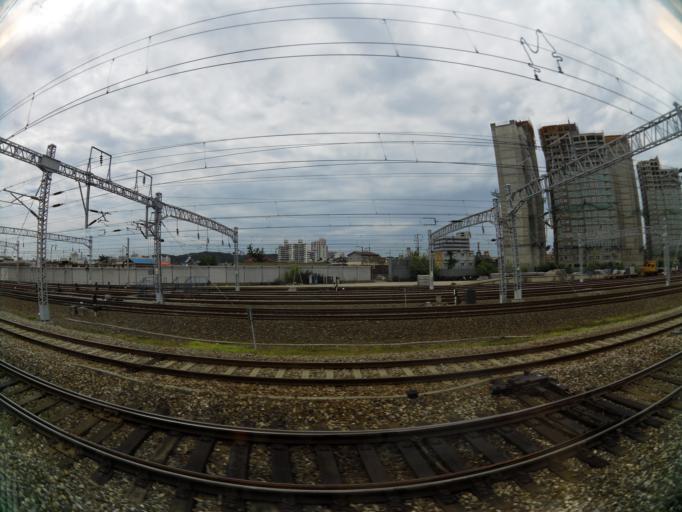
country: KR
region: Chungcheongnam-do
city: Cheonan
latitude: 36.8163
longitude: 127.1481
